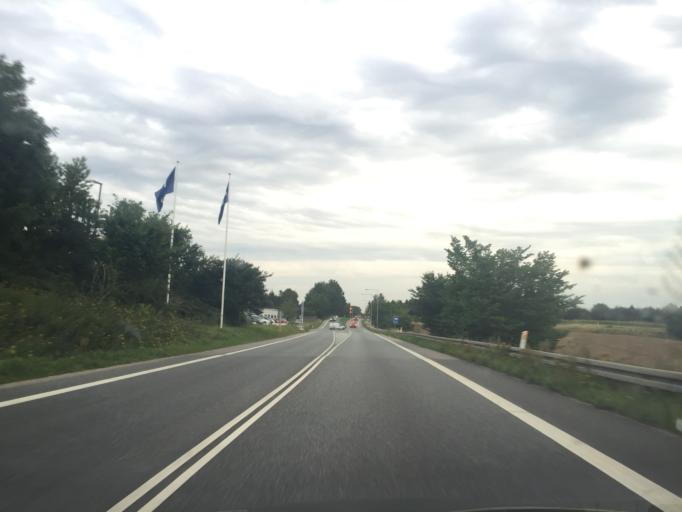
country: DK
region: Capital Region
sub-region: Egedal Kommune
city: Olstykke
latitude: 55.7666
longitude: 12.1438
